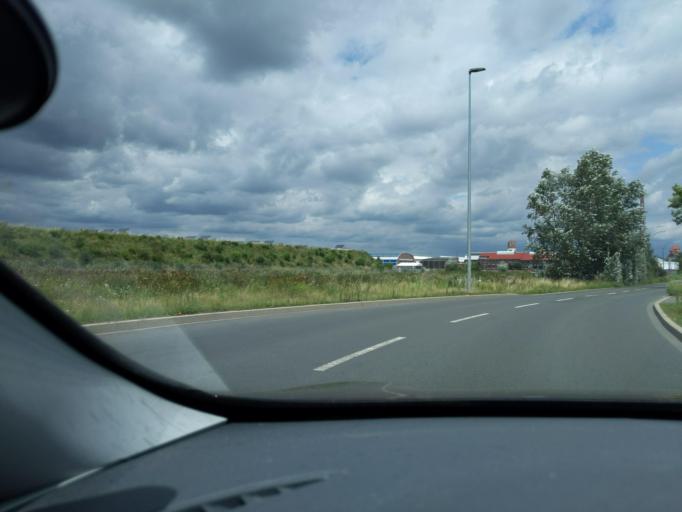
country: DE
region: North Rhine-Westphalia
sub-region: Regierungsbezirk Dusseldorf
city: Meerbusch
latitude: 51.2400
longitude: 6.7096
